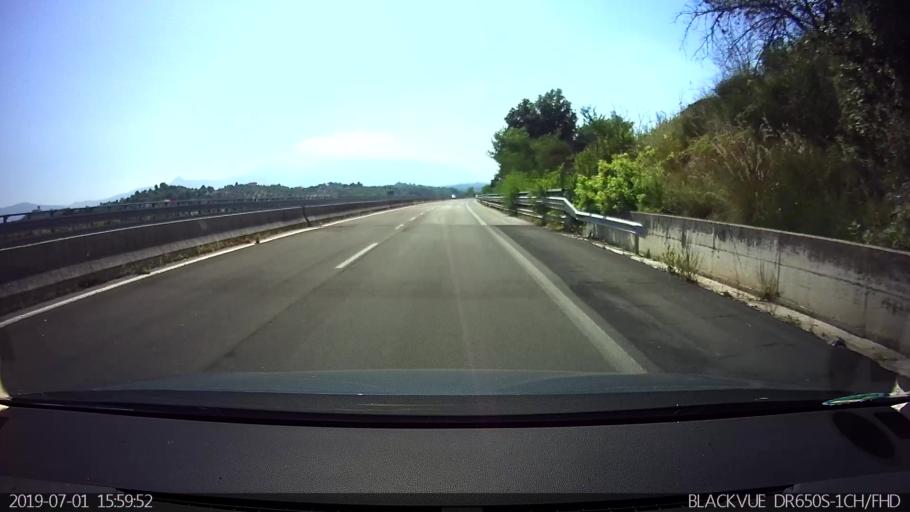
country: IT
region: Latium
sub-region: Provincia di Frosinone
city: Sant'Angelo in Villa-Giglio
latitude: 41.6614
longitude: 13.4108
